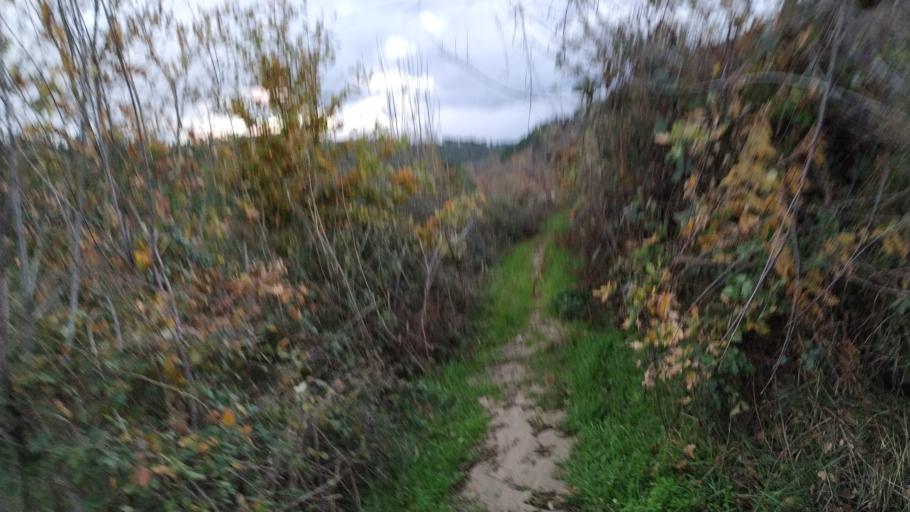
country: PT
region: Vila Real
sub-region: Vila Real
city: Vila Real
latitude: 41.3505
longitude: -7.7129
